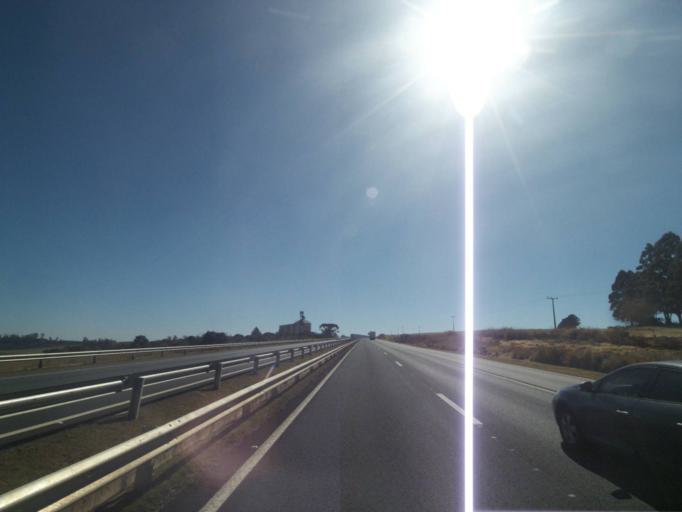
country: BR
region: Parana
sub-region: Tibagi
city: Tibagi
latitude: -24.8310
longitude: -50.4780
